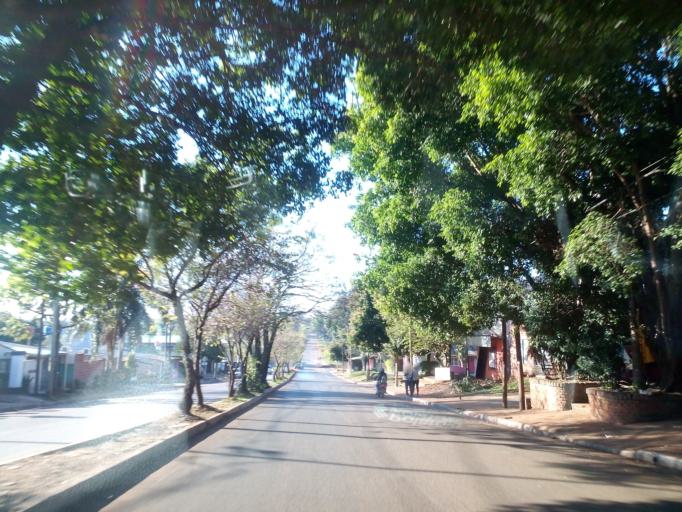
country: AR
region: Misiones
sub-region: Departamento de Capital
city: Posadas
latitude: -27.3951
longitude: -55.9359
